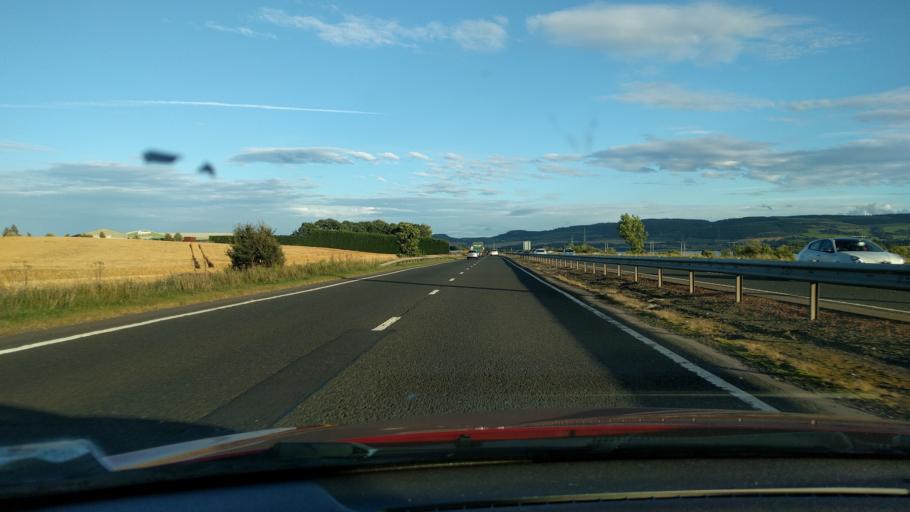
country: GB
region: Scotland
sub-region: Perth and Kinross
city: Abernethy
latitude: 56.3772
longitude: -3.3402
